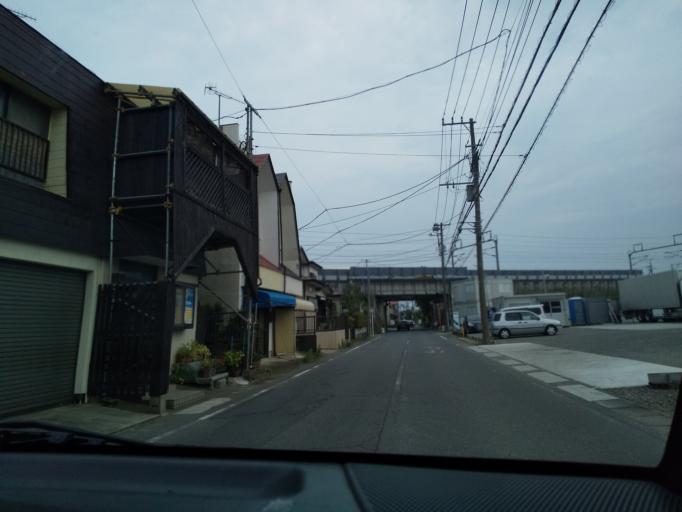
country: JP
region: Kanagawa
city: Atsugi
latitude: 35.3970
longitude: 139.3850
